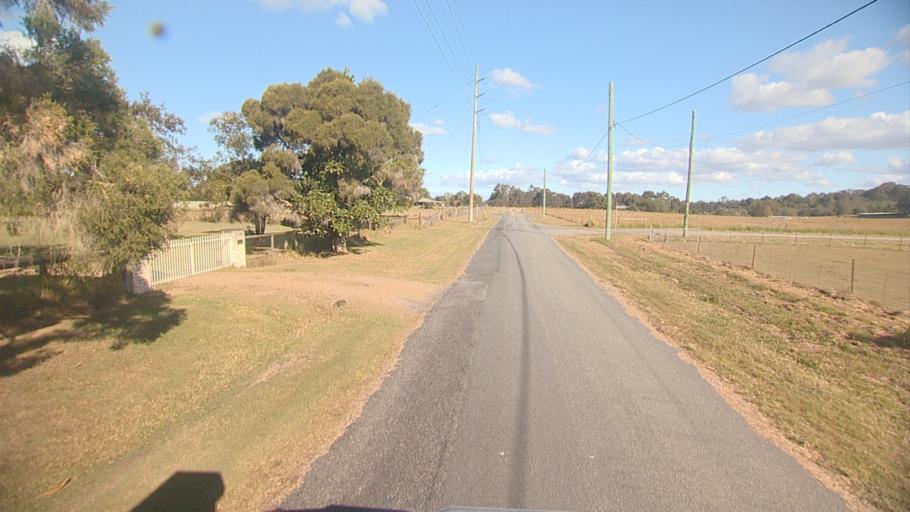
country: AU
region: Queensland
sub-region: Logan
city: Logan Reserve
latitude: -27.7246
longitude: 153.1139
